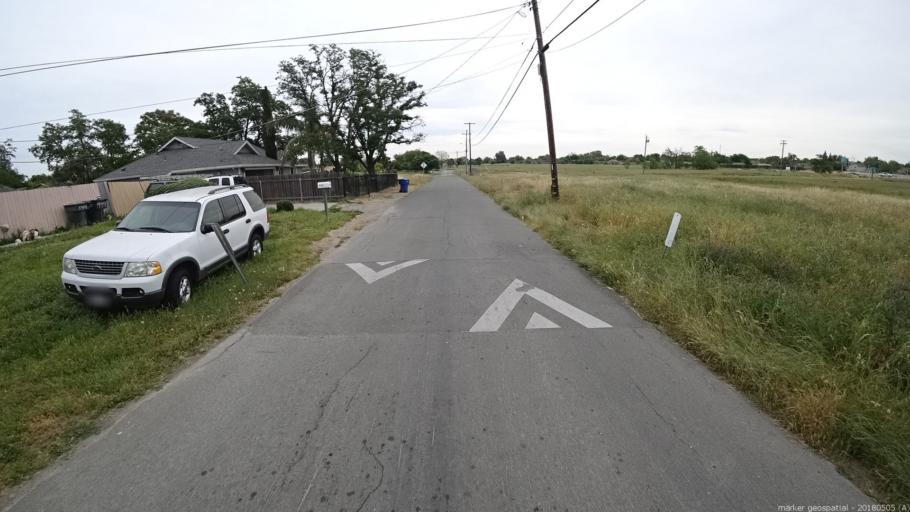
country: US
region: California
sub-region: Sacramento County
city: Rio Linda
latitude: 38.6439
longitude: -121.4442
